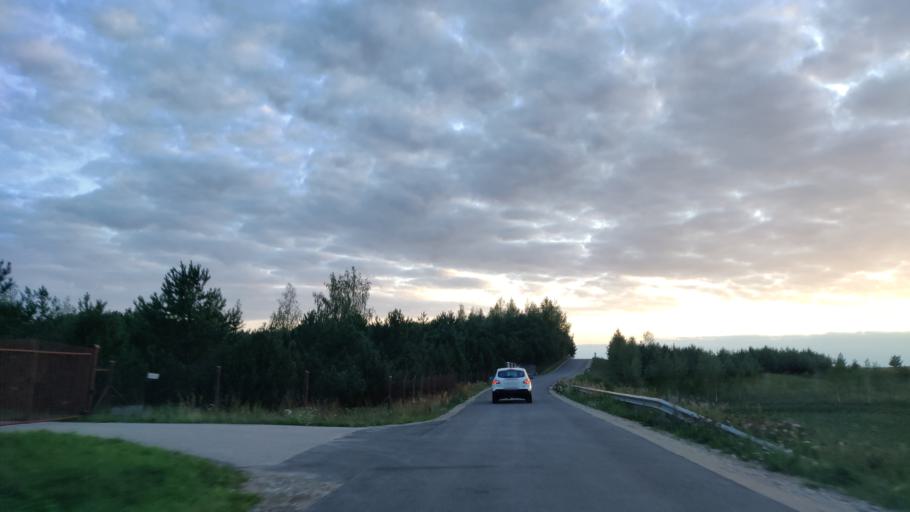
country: LT
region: Vilnius County
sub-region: Trakai
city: Rudiskes
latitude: 54.6084
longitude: 24.8051
